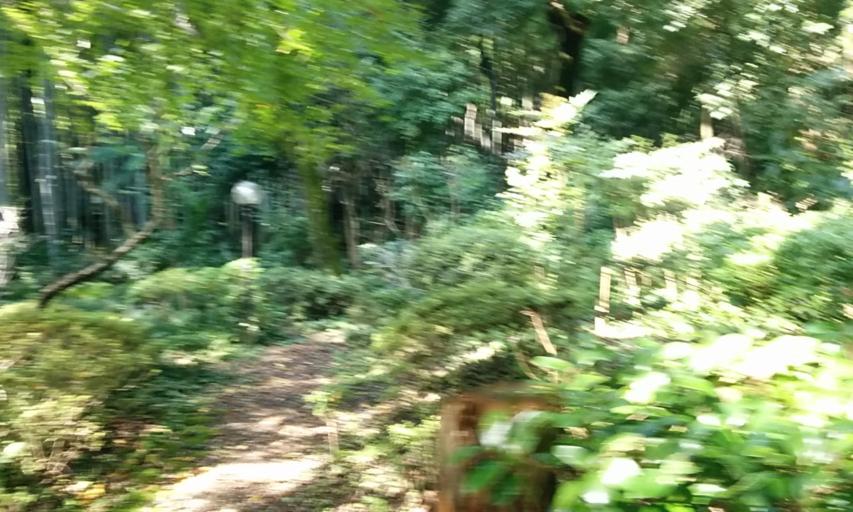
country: JP
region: Tokyo
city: Kokubunji
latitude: 35.6938
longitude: 139.4725
